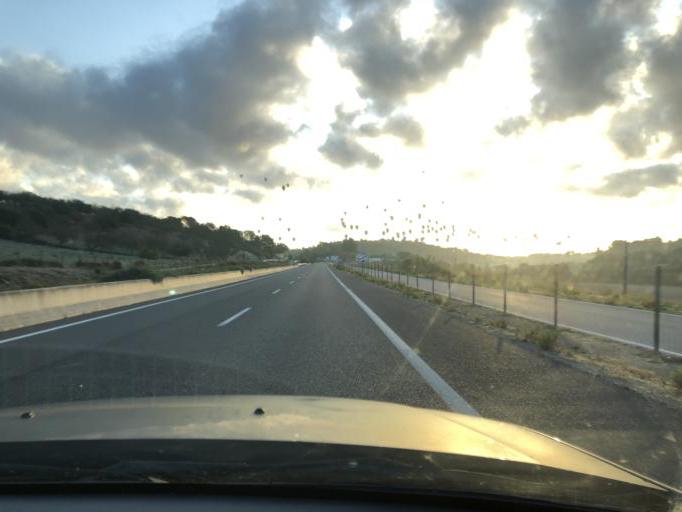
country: ES
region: Balearic Islands
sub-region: Illes Balears
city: Sant Joan
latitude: 39.5642
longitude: 3.0489
